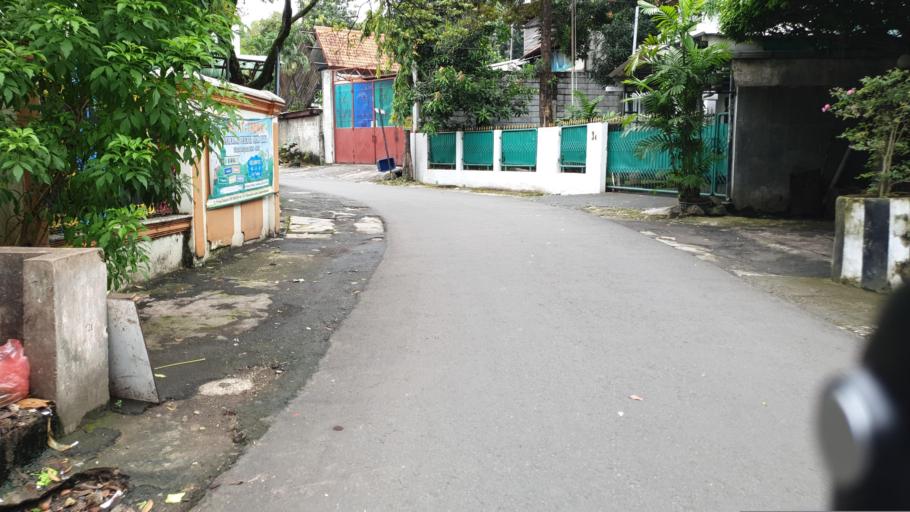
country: ID
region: Banten
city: South Tangerang
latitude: -6.2549
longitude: 106.7823
